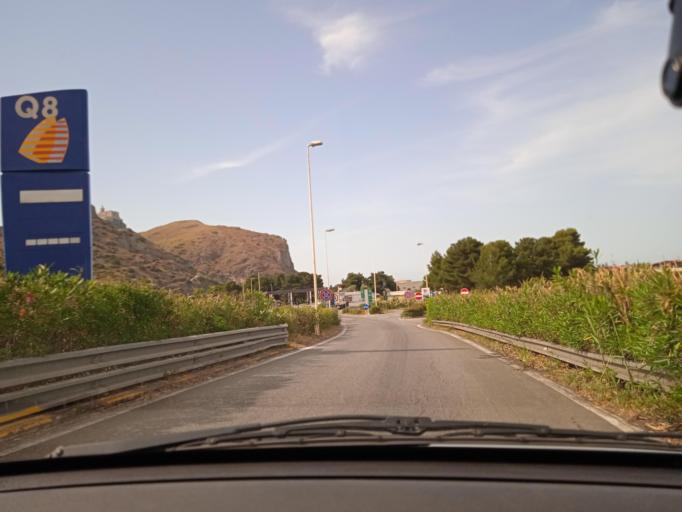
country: IT
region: Sicily
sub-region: Messina
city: Oliveri
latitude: 38.1262
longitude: 15.0538
